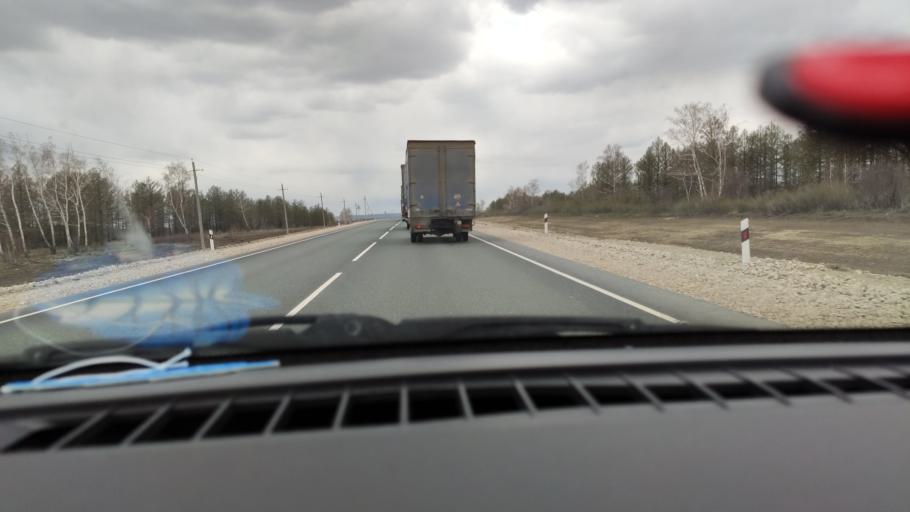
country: RU
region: Saratov
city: Shikhany
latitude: 52.1605
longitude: 47.0902
